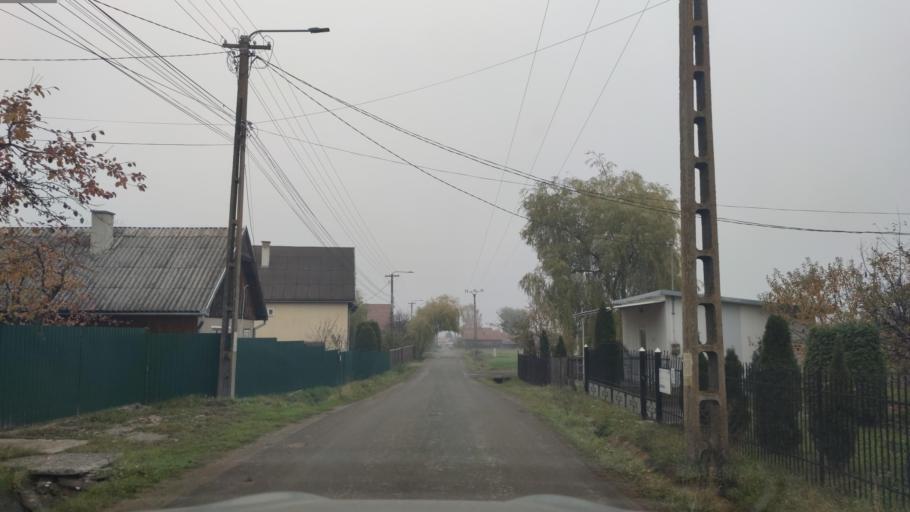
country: RO
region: Harghita
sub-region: Comuna Remetea
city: Remetea
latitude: 46.8052
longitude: 25.4441
